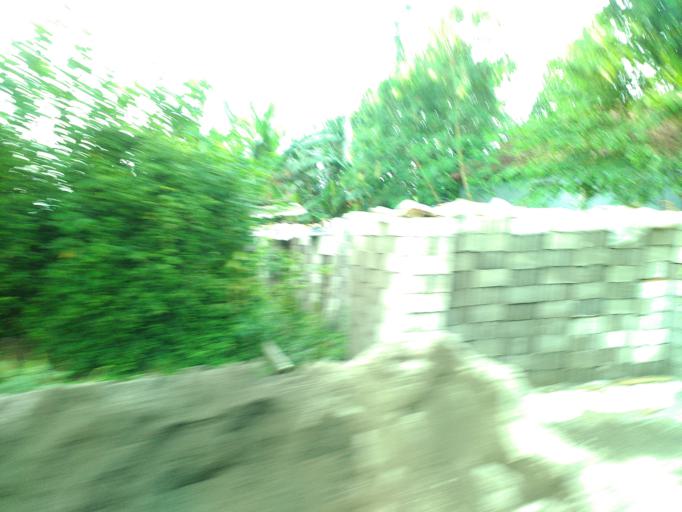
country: ID
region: Central Java
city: Ceper
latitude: -7.6768
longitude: 110.6475
